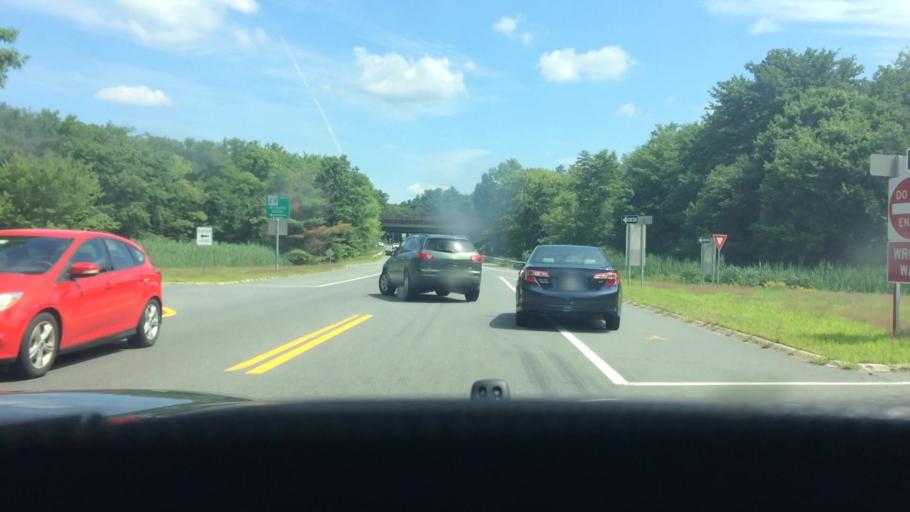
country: US
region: Massachusetts
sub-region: Middlesex County
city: North Reading
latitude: 42.6042
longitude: -71.1242
